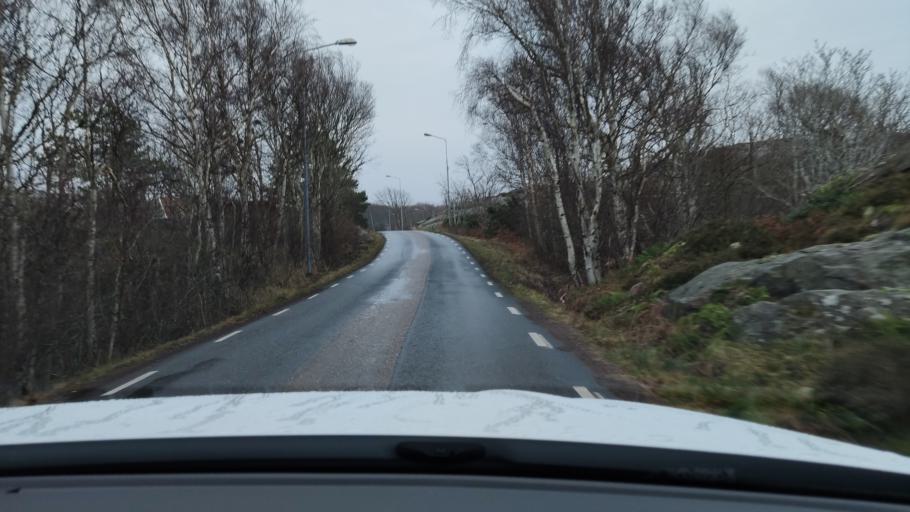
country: SE
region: Vaestra Goetaland
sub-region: Lysekils Kommun
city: Lysekil
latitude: 58.3234
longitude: 11.4080
